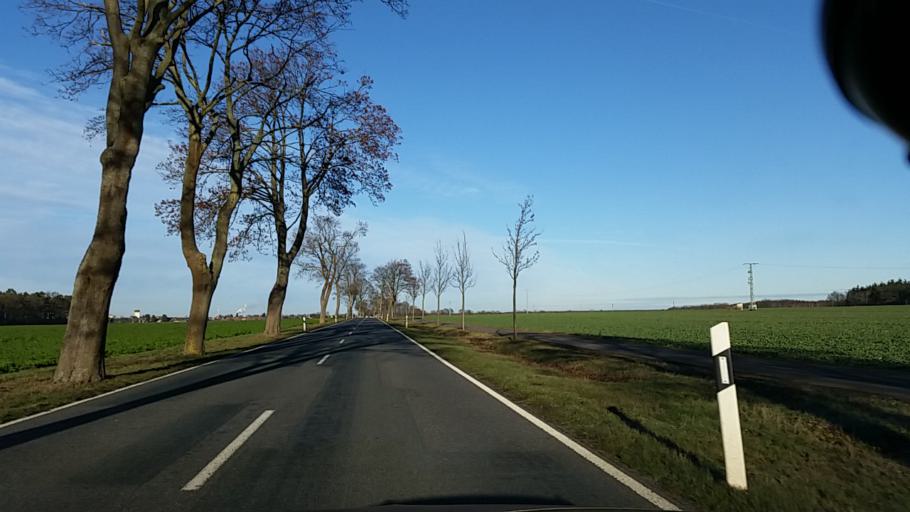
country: DE
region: Lower Saxony
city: Brome
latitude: 52.5814
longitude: 10.9321
